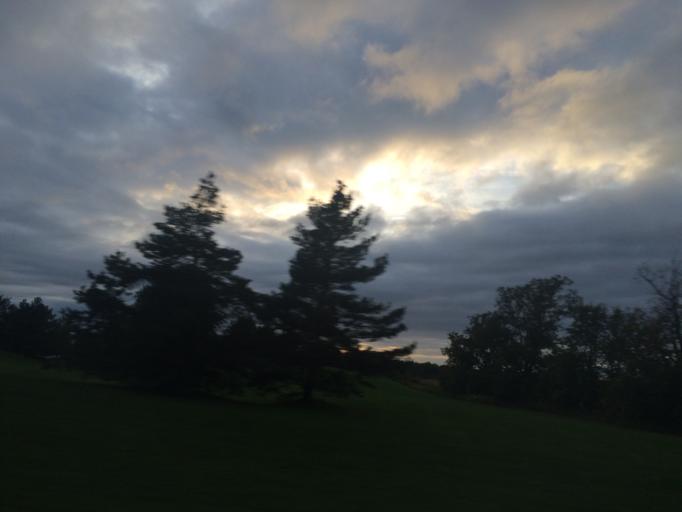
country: US
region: New York
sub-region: Erie County
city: Elma Center
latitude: 42.8094
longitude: -78.6368
